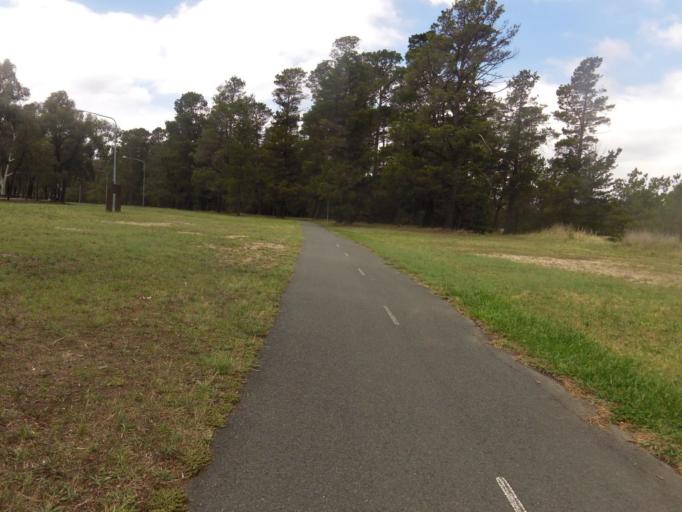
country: AU
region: Australian Capital Territory
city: Macarthur
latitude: -35.4140
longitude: 149.1165
